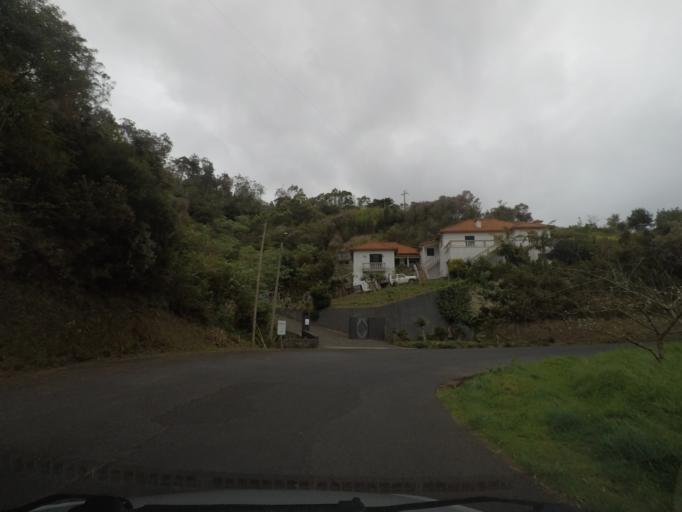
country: PT
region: Madeira
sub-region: Santa Cruz
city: Santa Cruz
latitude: 32.7445
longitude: -16.8254
